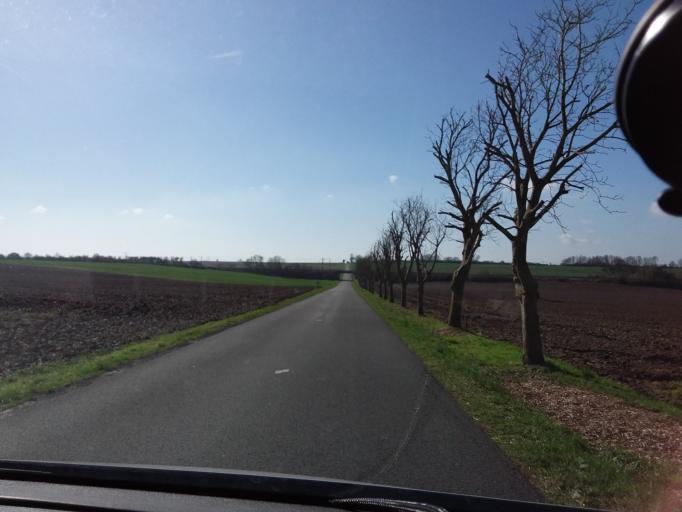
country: FR
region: Picardie
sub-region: Departement de l'Aisne
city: Hirson
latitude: 49.9009
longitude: 4.0989
